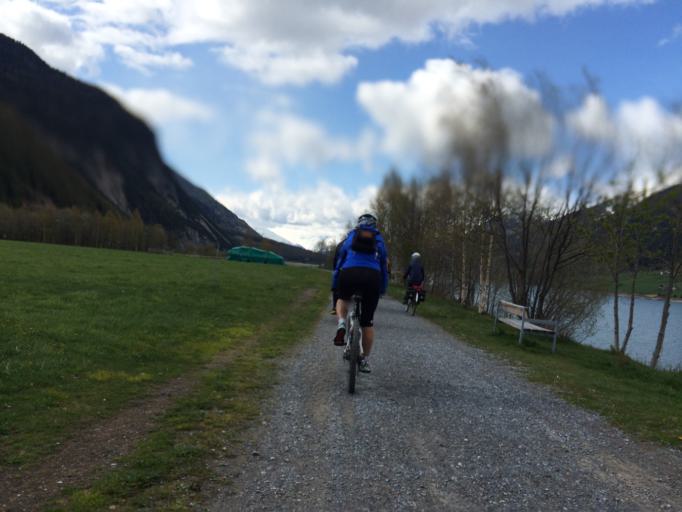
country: IT
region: Trentino-Alto Adige
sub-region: Bolzano
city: Curon Venosta
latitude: 46.8080
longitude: 10.5361
